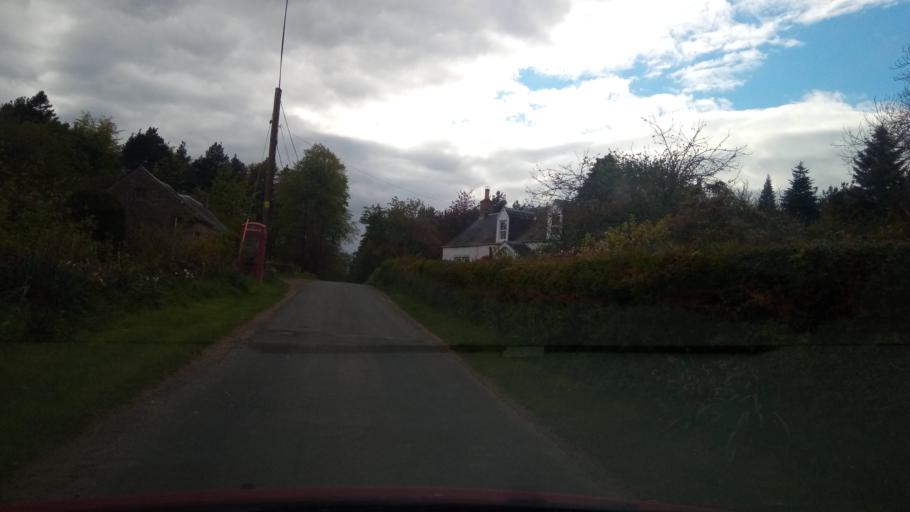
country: GB
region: Scotland
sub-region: The Scottish Borders
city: Saint Boswells
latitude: 55.5092
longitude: -2.6523
